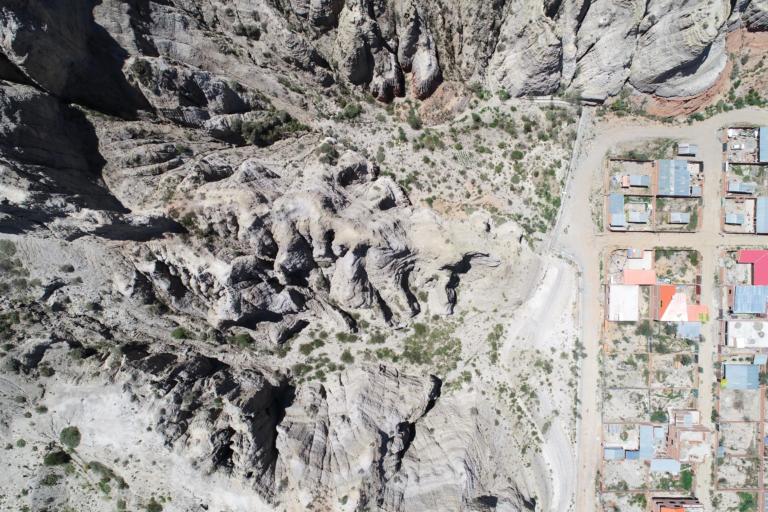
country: BO
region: La Paz
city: La Paz
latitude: -16.5147
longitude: -68.1031
